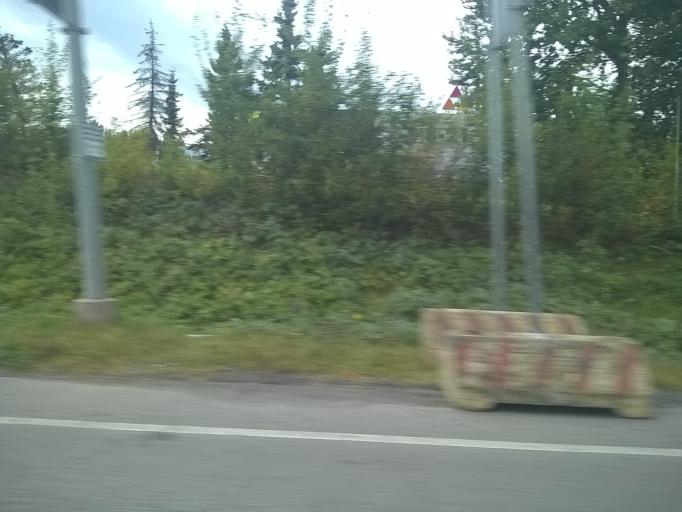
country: FI
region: Pirkanmaa
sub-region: Tampere
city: Tampere
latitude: 61.4896
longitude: 23.8235
